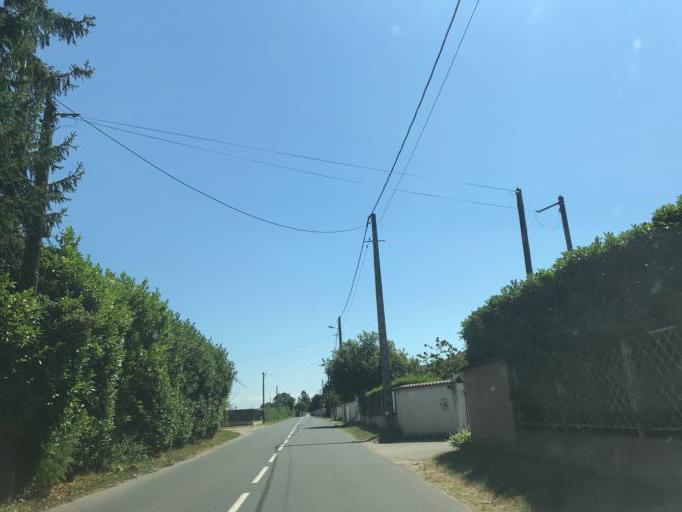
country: FR
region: Rhone-Alpes
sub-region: Departement de l'Ain
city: Saint-Didier-de-Formans
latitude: 45.9495
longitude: 4.8045
